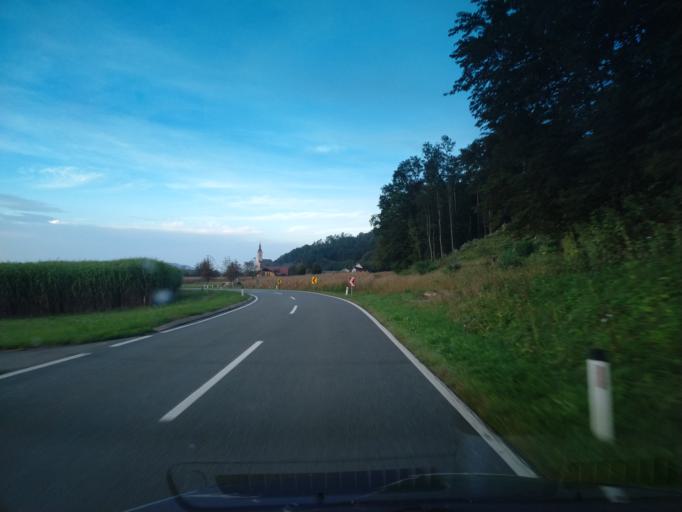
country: AT
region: Styria
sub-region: Politischer Bezirk Leibnitz
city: Sankt Johann im Saggautal
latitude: 46.6957
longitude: 15.3963
